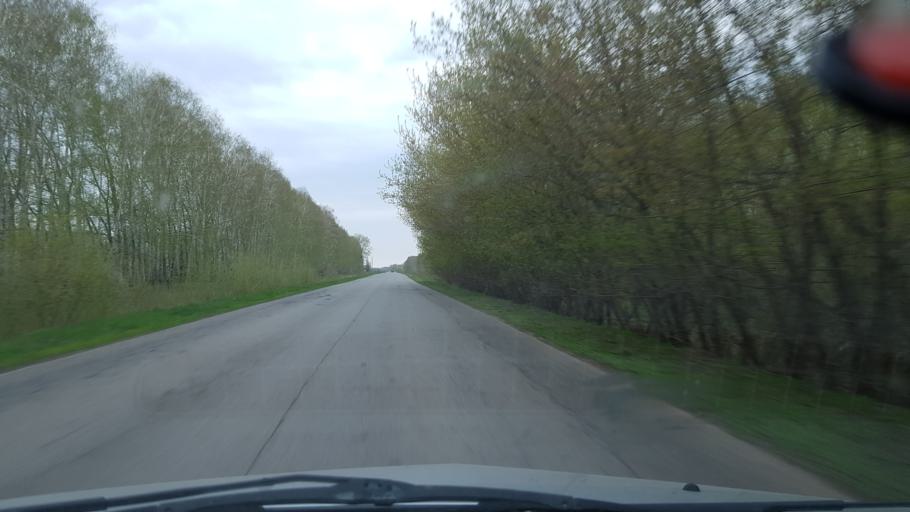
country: RU
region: Samara
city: Podstepki
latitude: 53.6651
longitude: 49.1735
